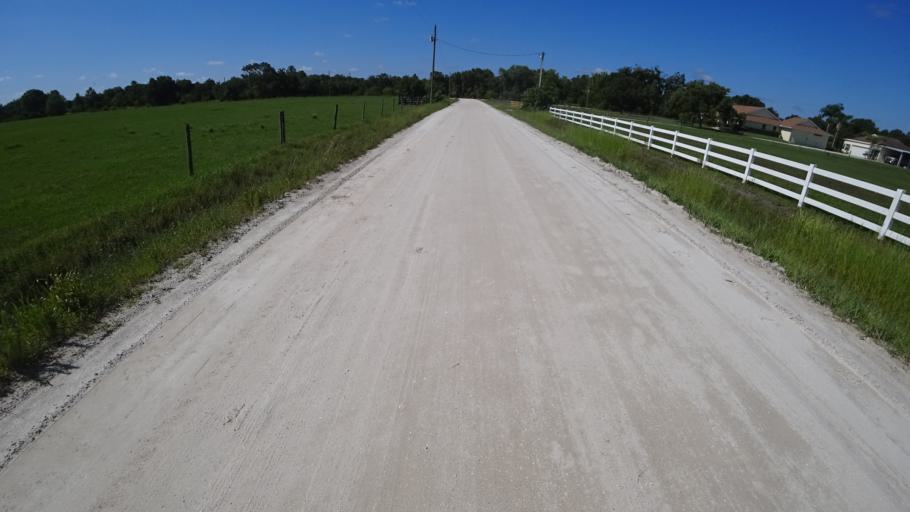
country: US
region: Florida
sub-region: Sarasota County
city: The Meadows
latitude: 27.4323
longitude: -82.3118
